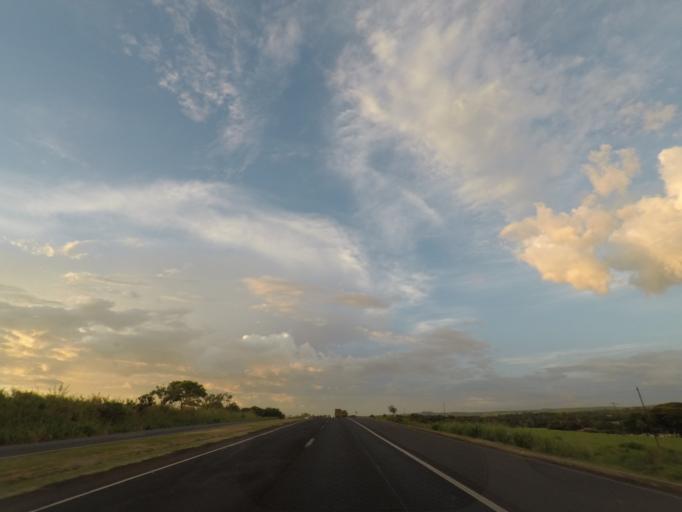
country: BR
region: Minas Gerais
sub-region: Uberaba
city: Uberaba
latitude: -19.6834
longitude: -47.9933
